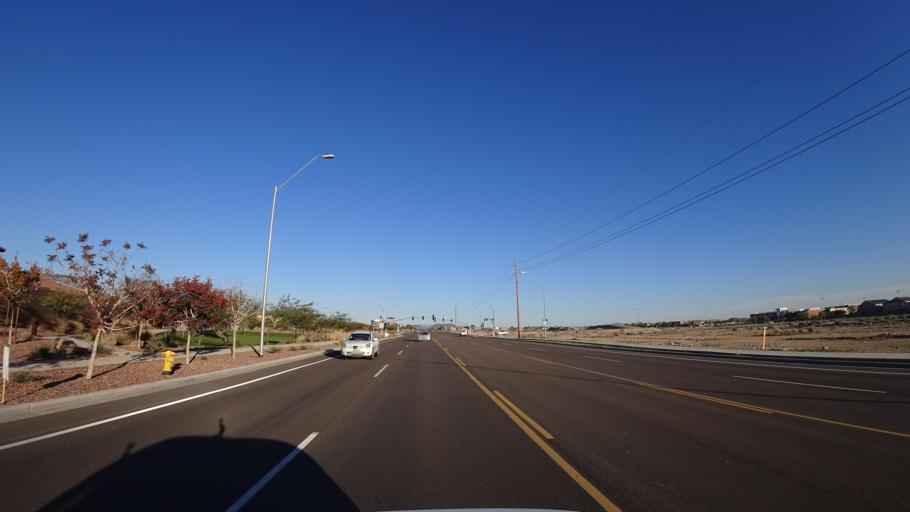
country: US
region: Arizona
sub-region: Maricopa County
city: Sun City West
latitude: 33.6818
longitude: -112.2716
